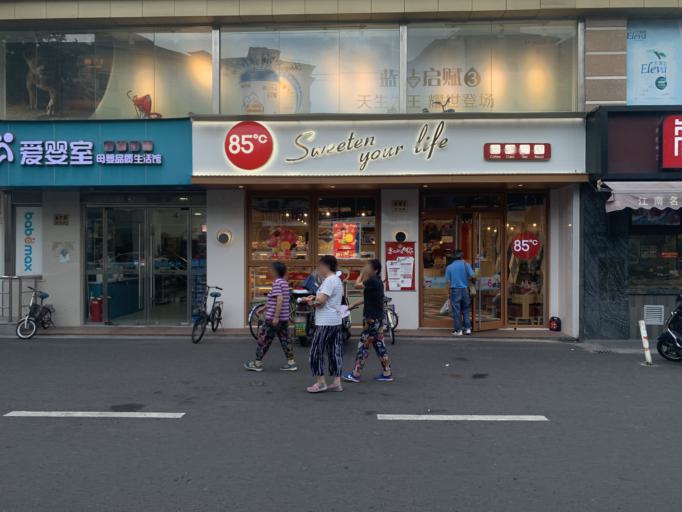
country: CN
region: Shanghai Shi
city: Pudong
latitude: 31.2513
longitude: 121.5756
